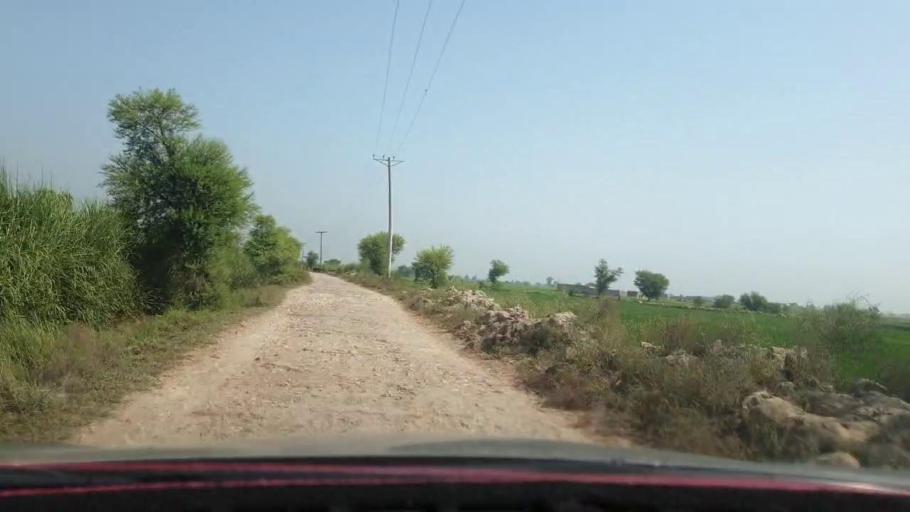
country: PK
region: Sindh
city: Warah
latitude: 27.4878
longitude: 67.8341
